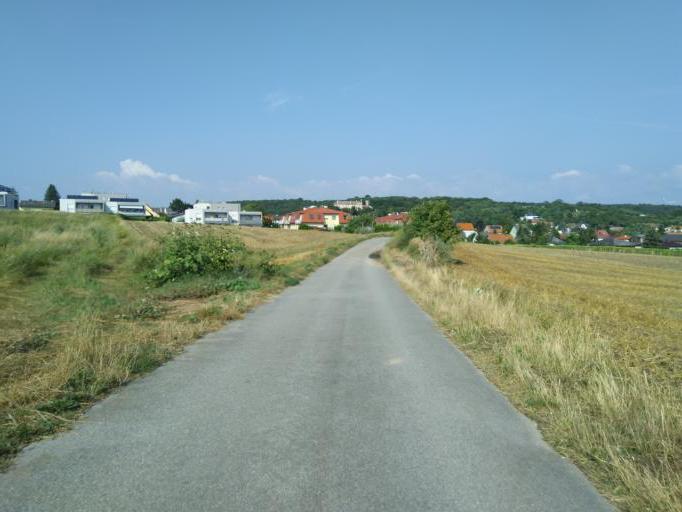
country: AT
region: Lower Austria
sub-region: Politischer Bezirk Ganserndorf
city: Gross-Schweinbarth
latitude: 48.3997
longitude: 16.6869
